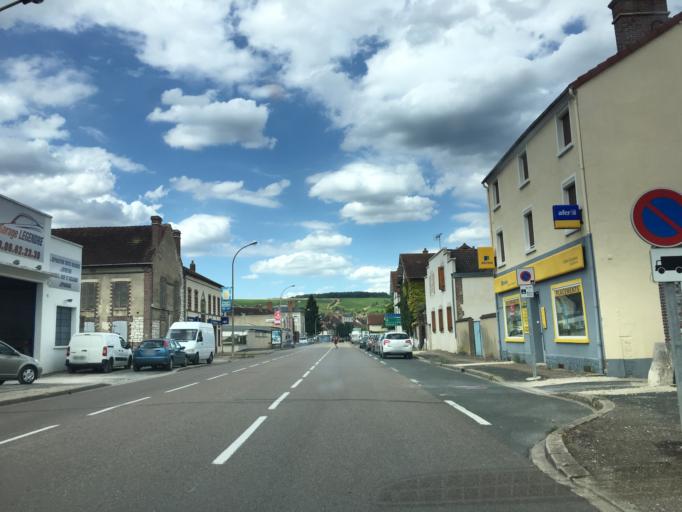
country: FR
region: Bourgogne
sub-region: Departement de l'Yonne
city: Joigny
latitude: 47.9747
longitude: 3.3947
